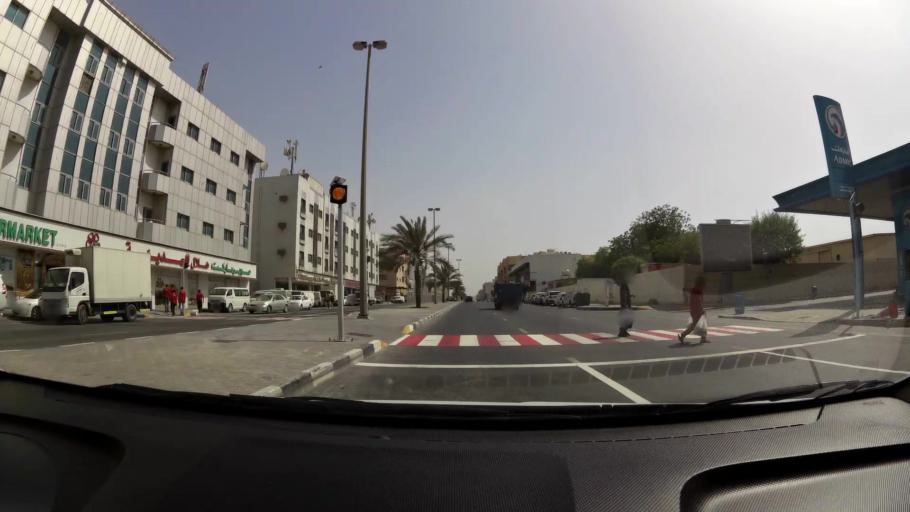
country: AE
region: Ash Shariqah
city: Sharjah
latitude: 25.3149
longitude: 55.4251
